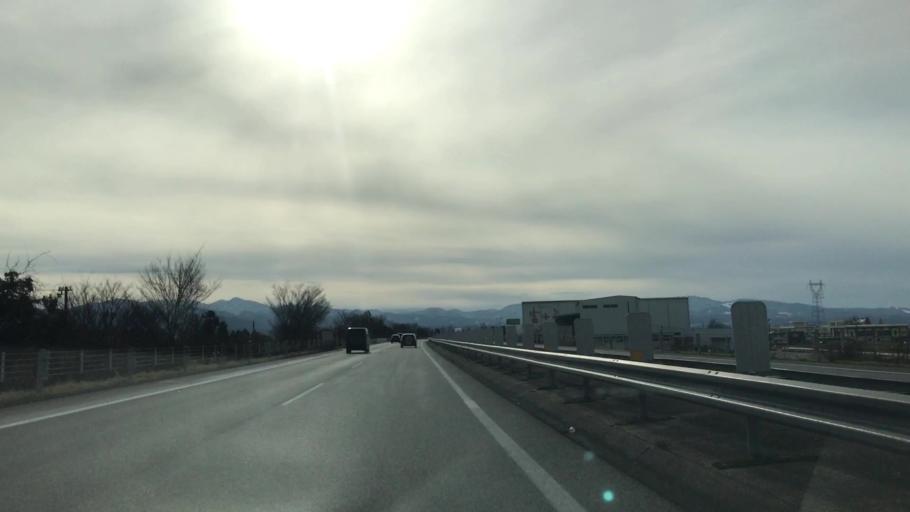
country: JP
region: Toyama
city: Toyama-shi
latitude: 36.6562
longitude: 137.2573
